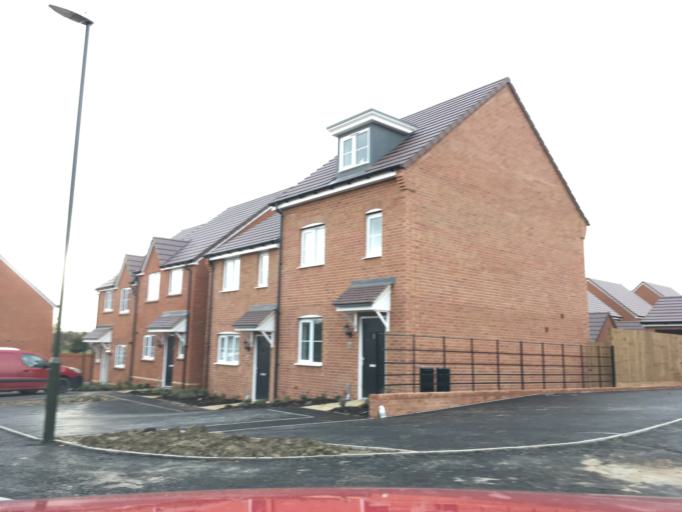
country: GB
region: England
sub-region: Worcestershire
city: Bredon
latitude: 51.9999
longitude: -2.0920
